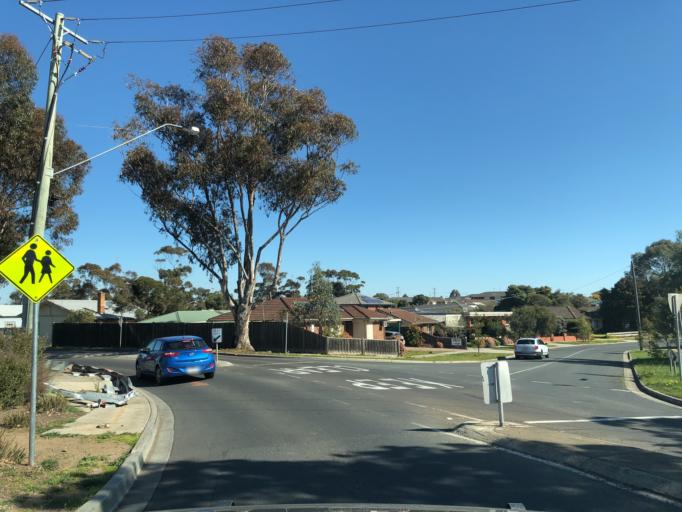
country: AU
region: Victoria
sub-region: Hume
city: Diggers Rest
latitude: -37.6268
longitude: 144.7197
